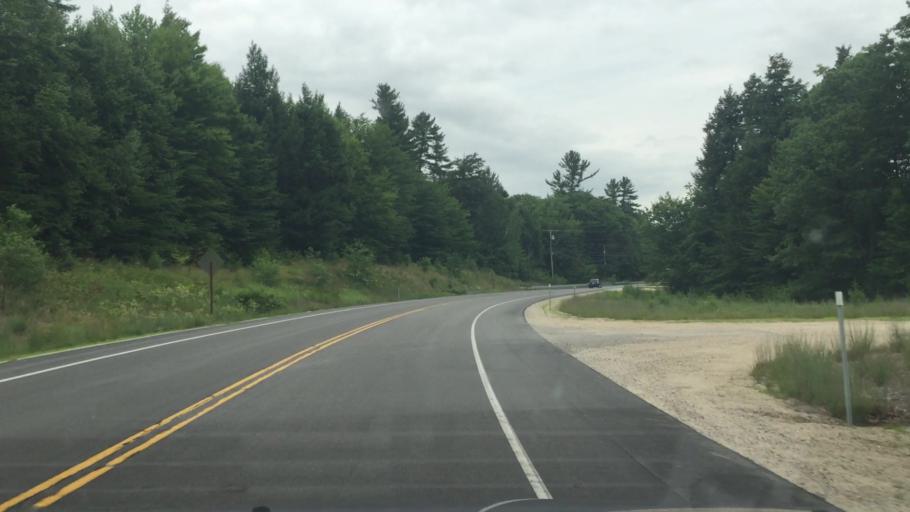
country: US
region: New Hampshire
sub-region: Carroll County
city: Tamworth
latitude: 43.8454
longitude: -71.2663
